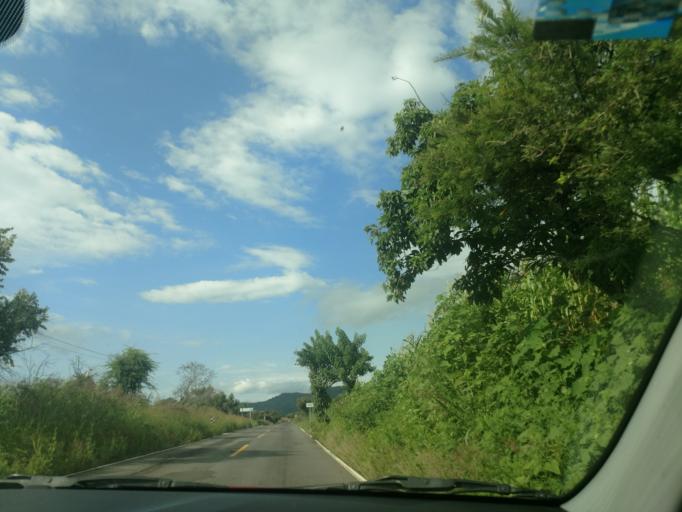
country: MX
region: Jalisco
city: Ameca
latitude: 20.5335
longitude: -104.2030
